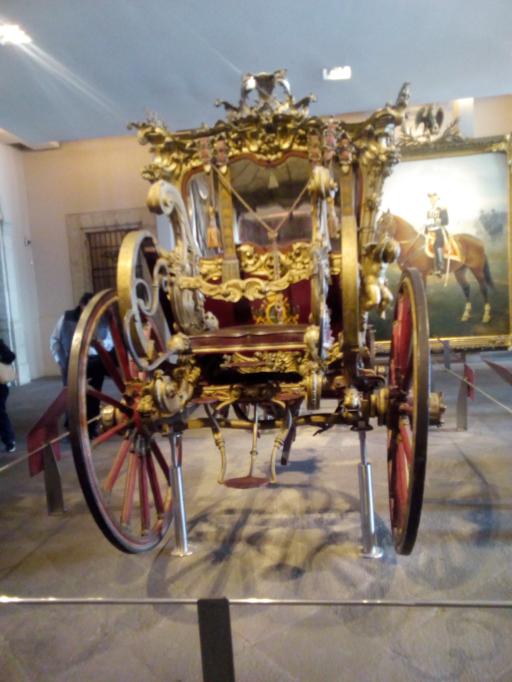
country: MX
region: Mexico City
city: Polanco
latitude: 19.4205
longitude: -99.1822
